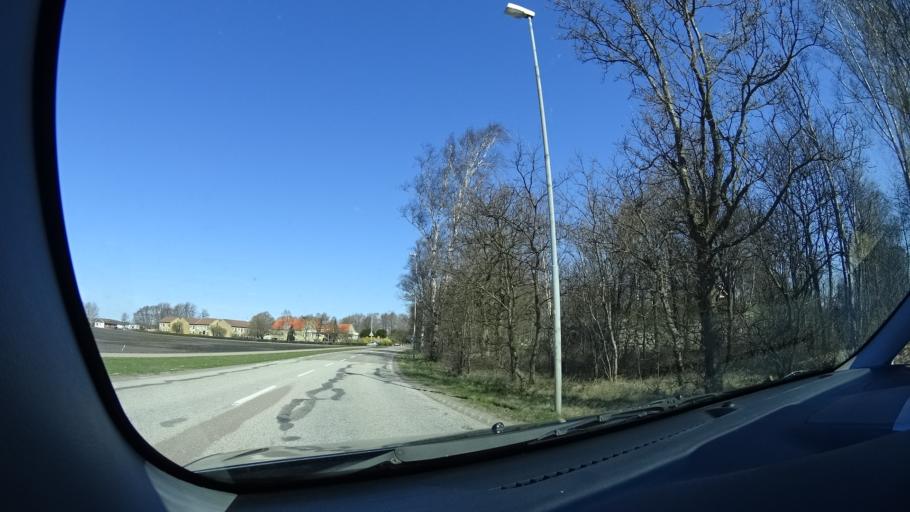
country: SE
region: Skane
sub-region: Hoganas Kommun
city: Hoganas
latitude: 56.2033
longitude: 12.5928
